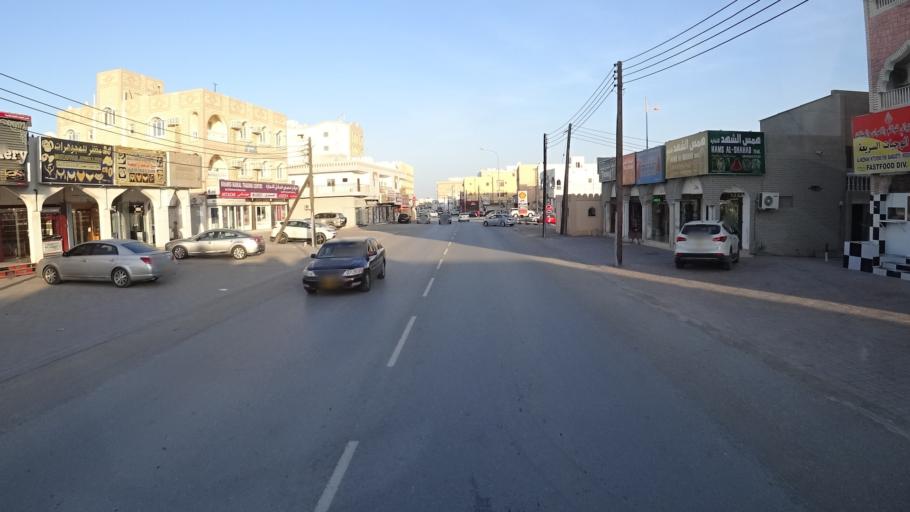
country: OM
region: Al Batinah
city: Barka'
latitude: 23.7072
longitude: 57.8892
